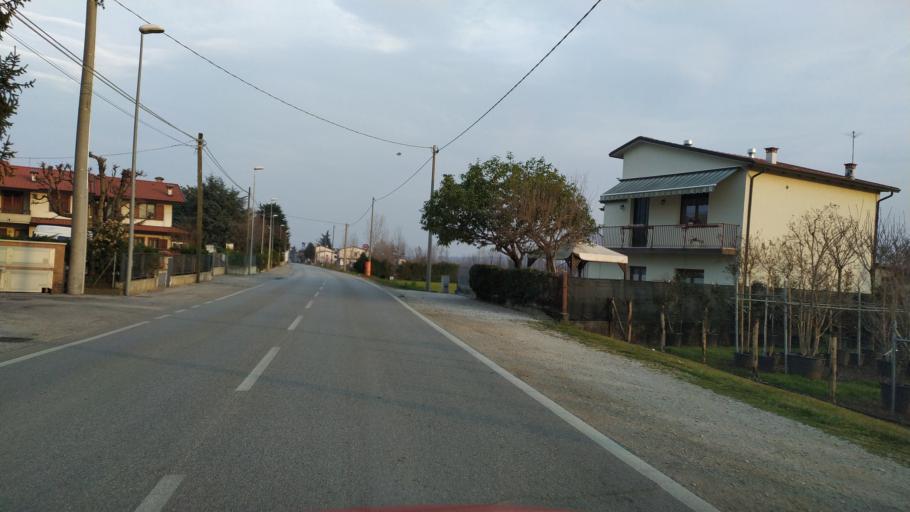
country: IT
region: Veneto
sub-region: Provincia di Vicenza
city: Sarcedo
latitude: 45.6892
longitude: 11.5095
